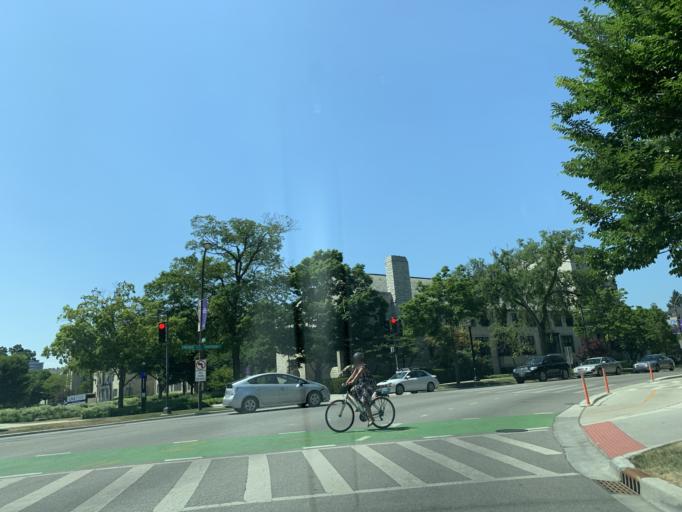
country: US
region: Illinois
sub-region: Cook County
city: Evanston
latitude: 42.0510
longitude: -87.6771
